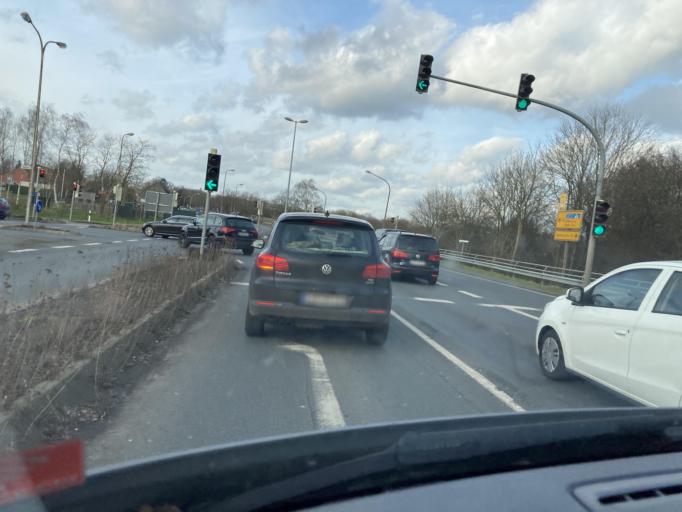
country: DE
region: Lower Saxony
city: Leer
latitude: 53.2226
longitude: 7.4826
